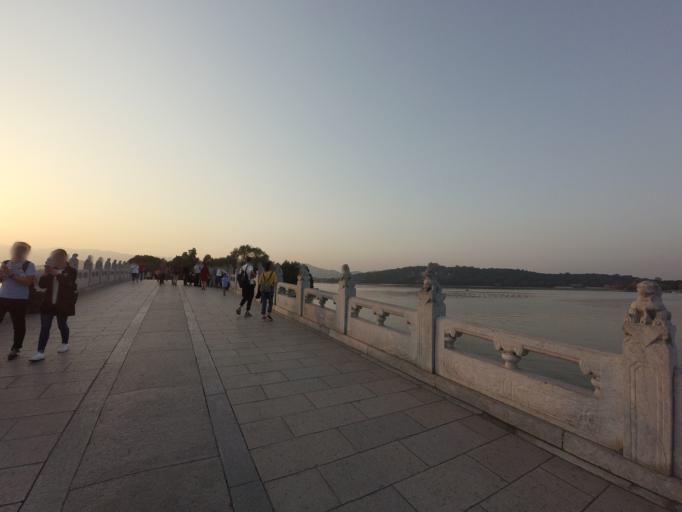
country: CN
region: Beijing
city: Haidian
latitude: 39.9894
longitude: 116.2719
